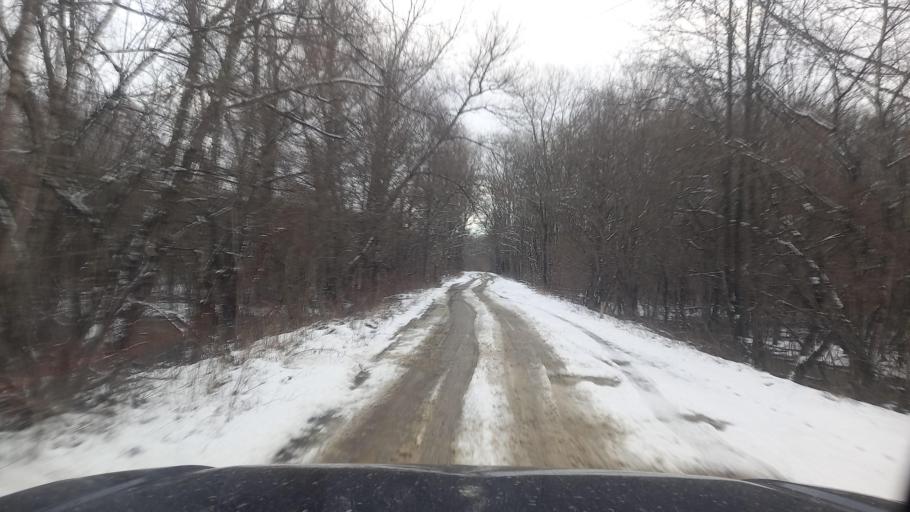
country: RU
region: Krasnodarskiy
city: Smolenskaya
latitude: 44.6743
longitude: 38.7501
